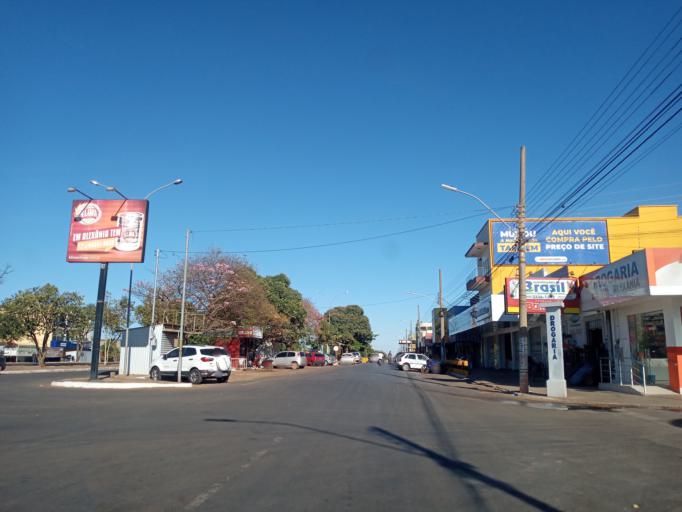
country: BR
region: Goias
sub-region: Abadiania
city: Abadiania
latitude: -16.0893
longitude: -48.5034
